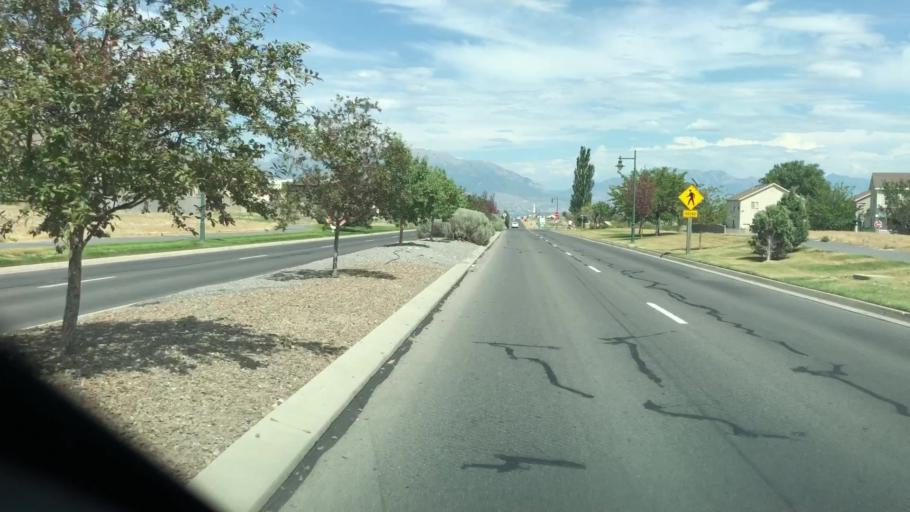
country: US
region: Utah
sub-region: Utah County
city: Eagle Mountain
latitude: 40.3621
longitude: -111.9707
